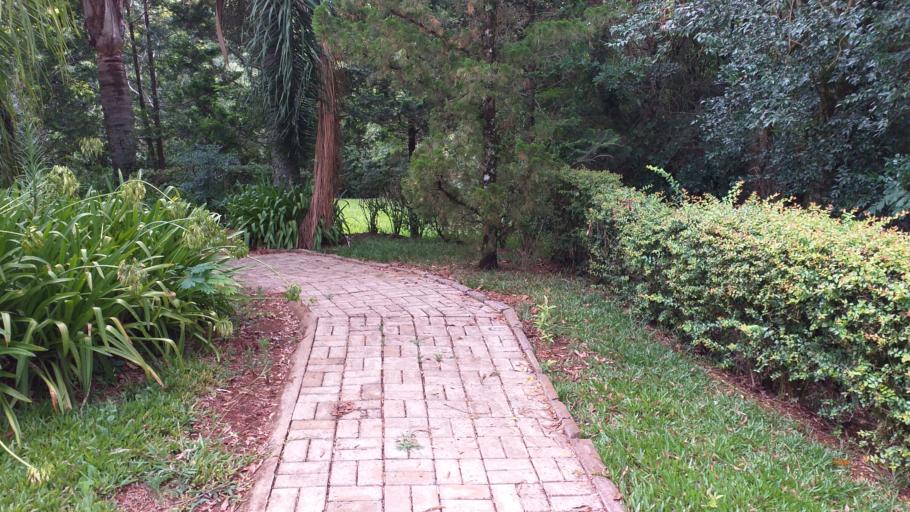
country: BR
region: Rio Grande do Sul
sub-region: Marau
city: Marau
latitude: -28.4427
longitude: -52.1889
